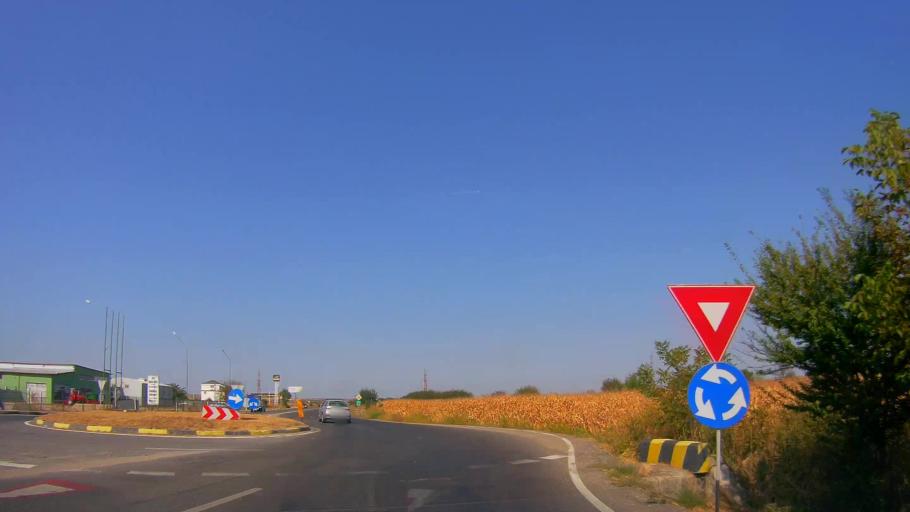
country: RO
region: Giurgiu
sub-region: Comuna Fratesti
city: Remus
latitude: 43.9490
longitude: 25.9805
